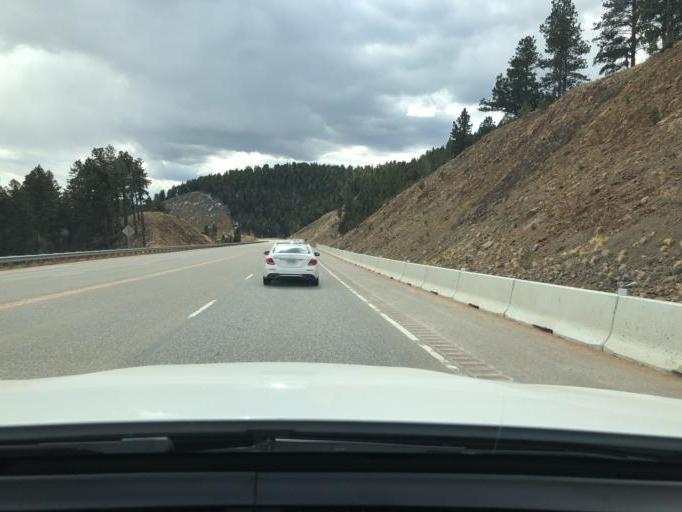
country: US
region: Colorado
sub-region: Clear Creek County
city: Idaho Springs
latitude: 39.7718
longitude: -105.4717
